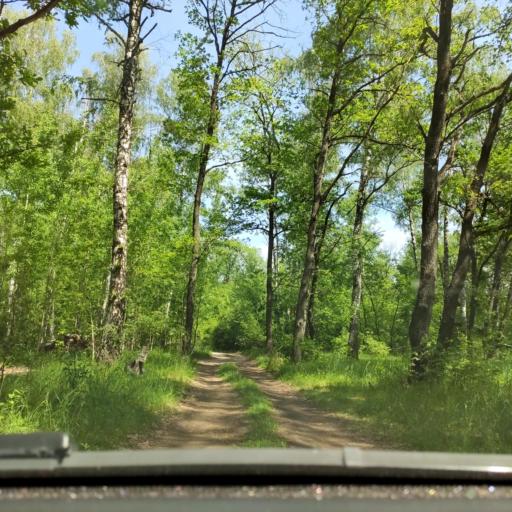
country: RU
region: Voronezj
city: Podgornoye
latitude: 51.8042
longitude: 39.1475
